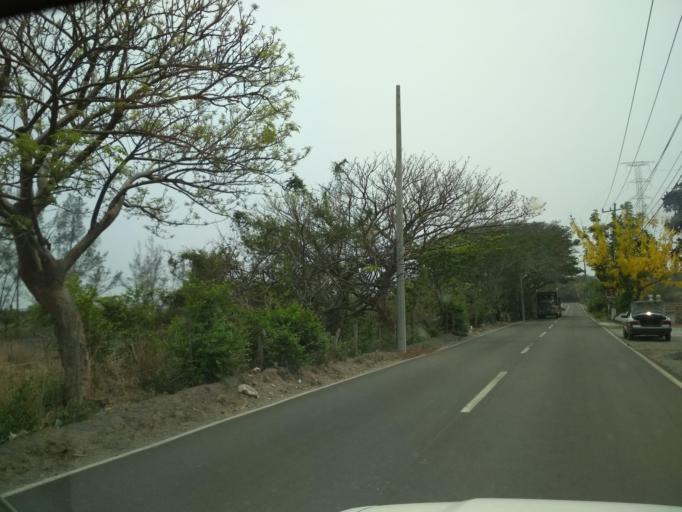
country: MX
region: Veracruz
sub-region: Veracruz
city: Las Amapolas
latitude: 19.1504
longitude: -96.2263
